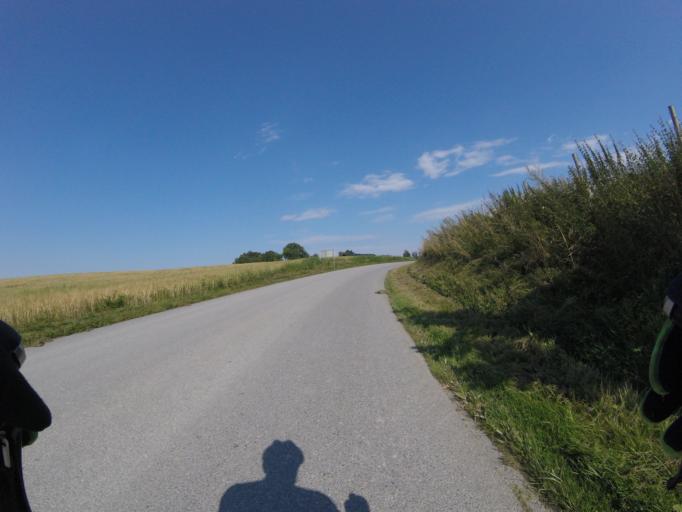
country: NO
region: Akershus
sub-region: Ullensaker
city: Klofta
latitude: 60.0973
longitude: 11.1739
